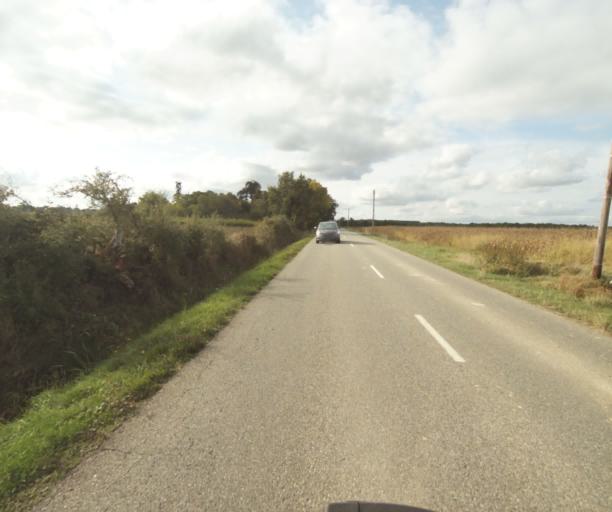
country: FR
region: Midi-Pyrenees
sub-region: Departement du Tarn-et-Garonne
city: Verdun-sur-Garonne
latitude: 43.8487
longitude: 1.1455
